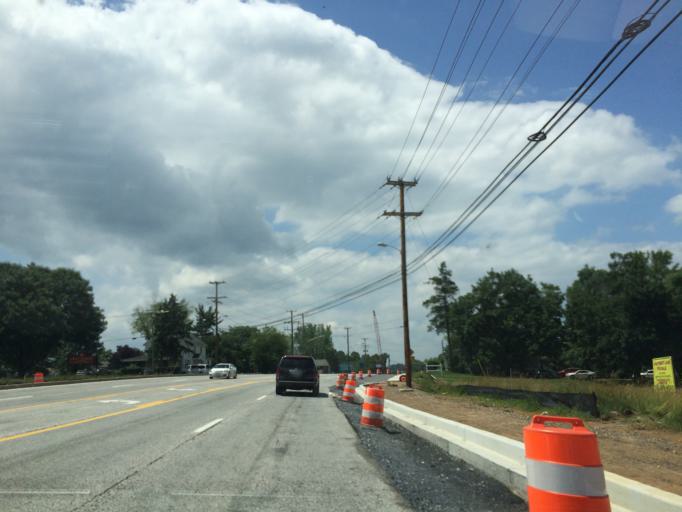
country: US
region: Maryland
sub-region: Baltimore County
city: Randallstown
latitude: 39.3758
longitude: -76.8137
